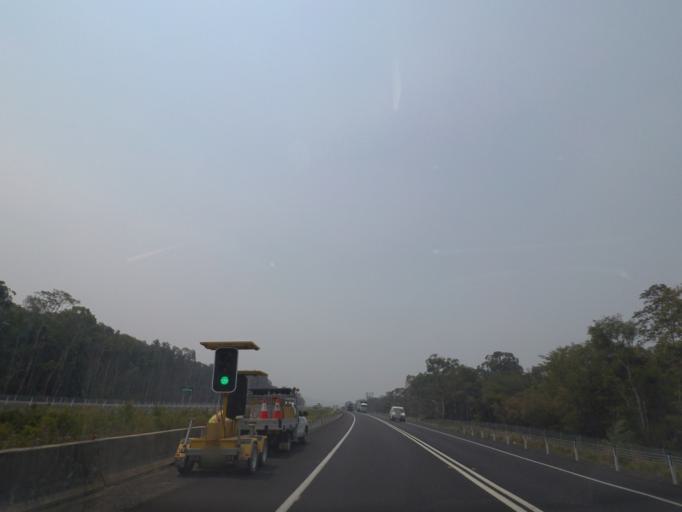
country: AU
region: New South Wales
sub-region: Ballina
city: Ballina
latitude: -28.9128
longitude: 153.4786
